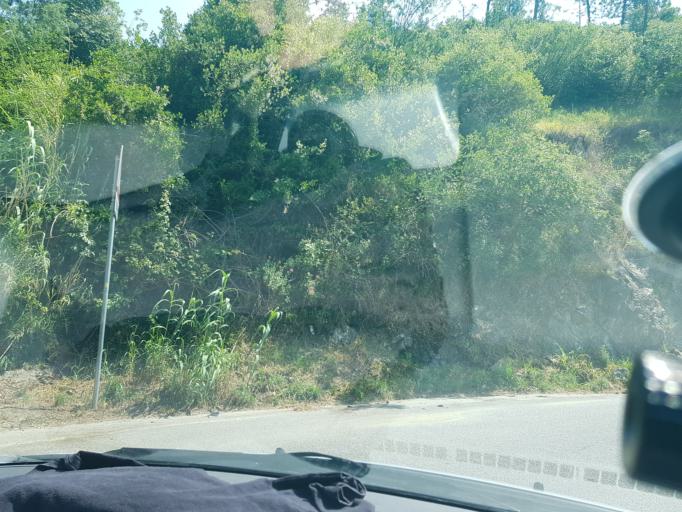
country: IT
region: Liguria
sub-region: Provincia di Genova
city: San Teodoro
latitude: 44.4379
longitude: 8.8405
